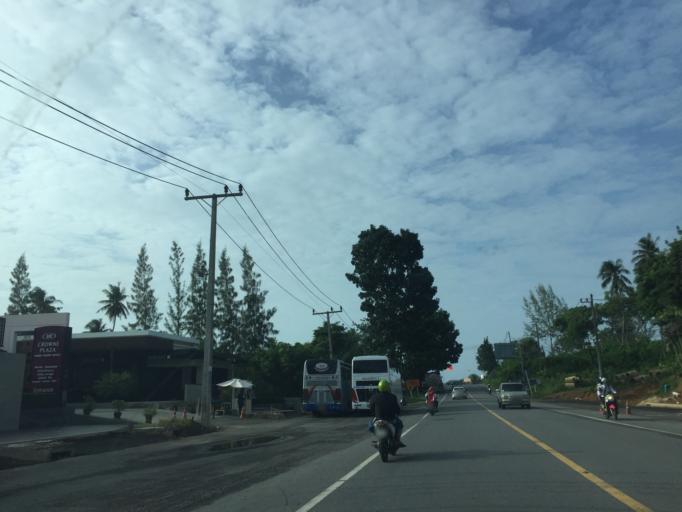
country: TH
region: Phuket
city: Mueang Phuket
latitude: 7.8320
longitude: 98.4005
